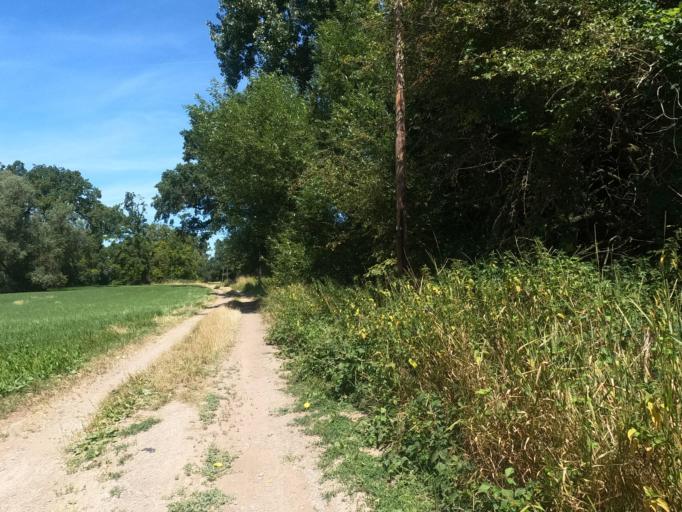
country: DE
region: Hesse
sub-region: Regierungsbezirk Darmstadt
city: Ginsheim-Gustavsburg
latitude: 49.9460
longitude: 8.3514
